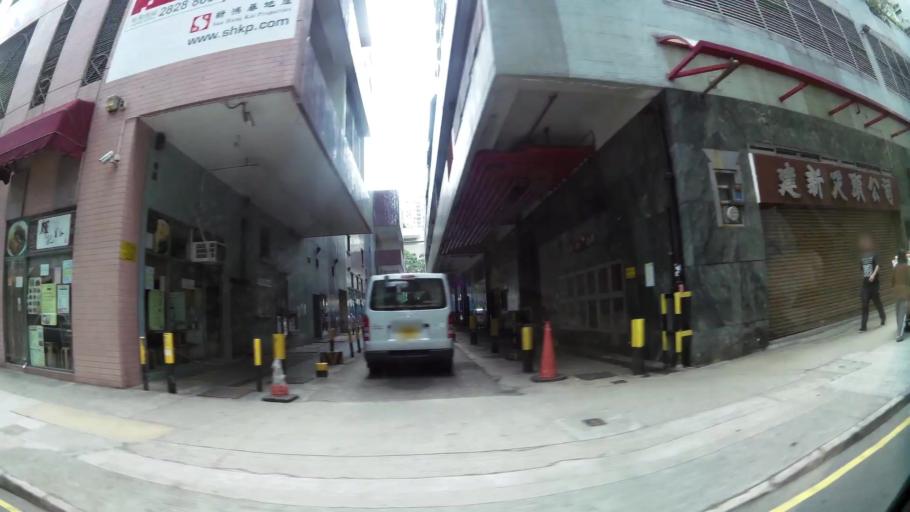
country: HK
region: Wong Tai Sin
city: Wong Tai Sin
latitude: 22.3367
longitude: 114.1977
